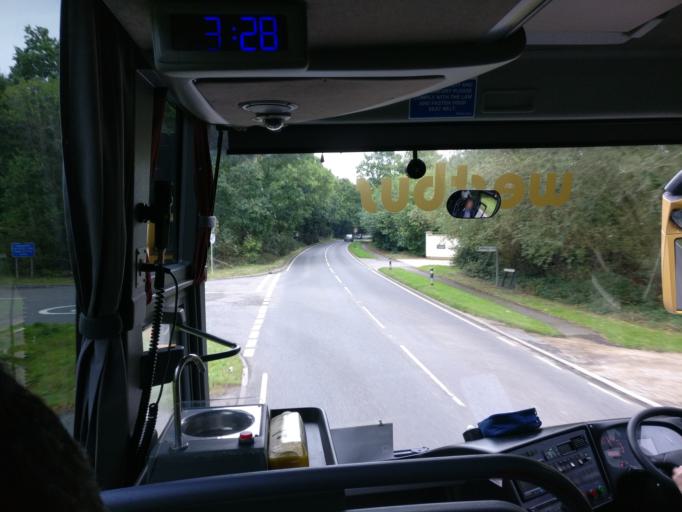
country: GB
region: England
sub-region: Surrey
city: Chobham
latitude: 51.3431
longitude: -0.5945
